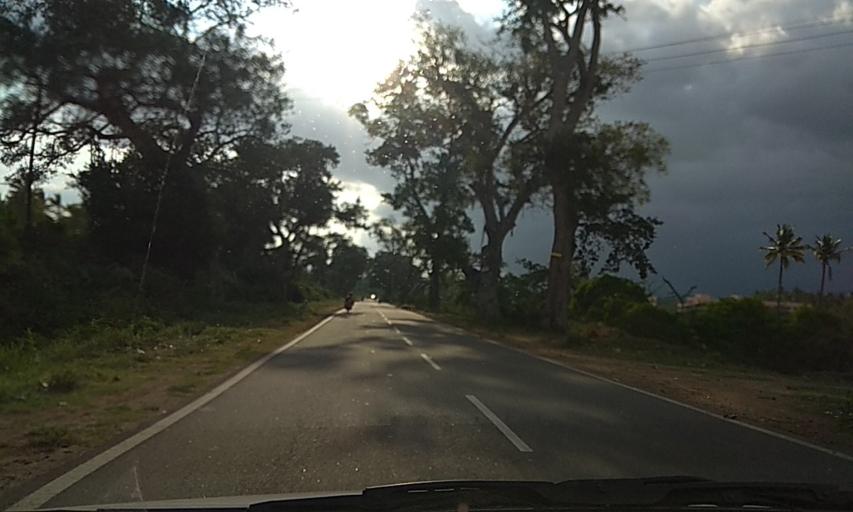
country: IN
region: Karnataka
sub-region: Chamrajnagar
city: Gundlupet
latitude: 11.8108
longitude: 76.7098
